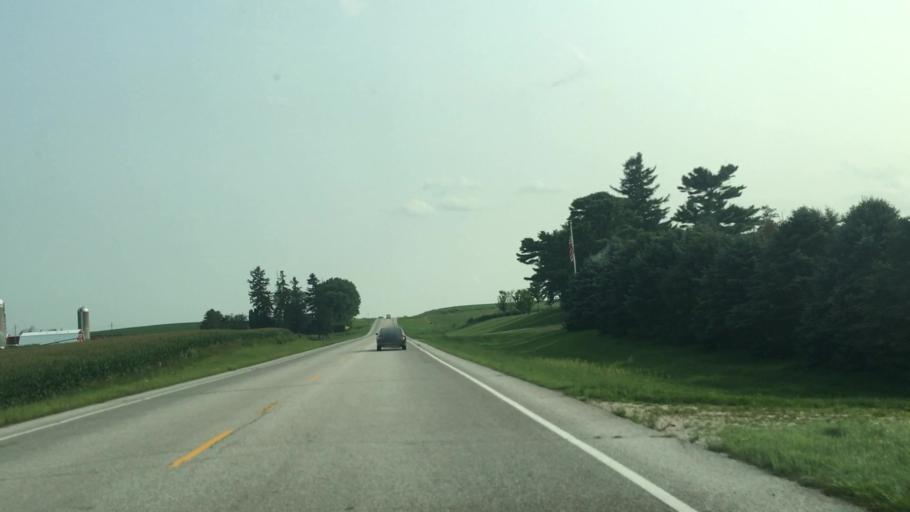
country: US
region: Minnesota
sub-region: Fillmore County
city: Harmony
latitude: 43.6057
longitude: -91.9298
